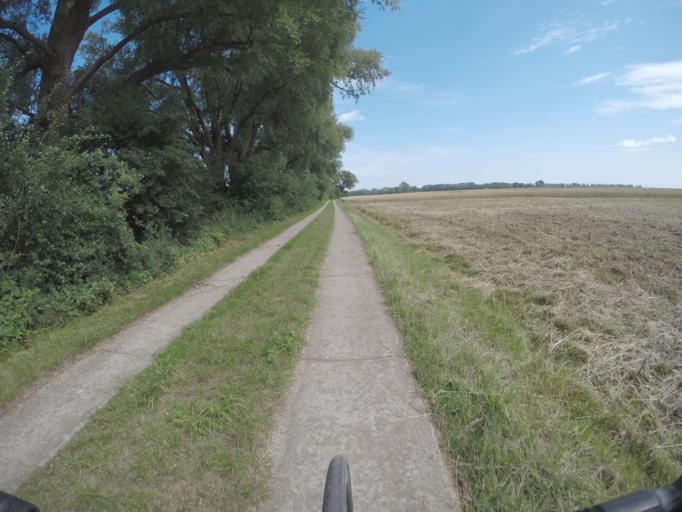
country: DE
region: Mecklenburg-Vorpommern
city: Altefahr
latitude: 54.3693
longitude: 13.1314
